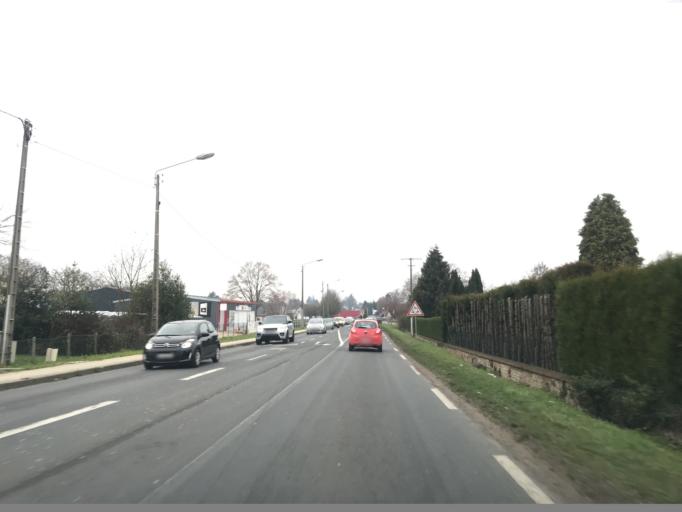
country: FR
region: Haute-Normandie
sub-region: Departement de la Seine-Maritime
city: Boos
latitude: 49.3980
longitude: 1.1774
